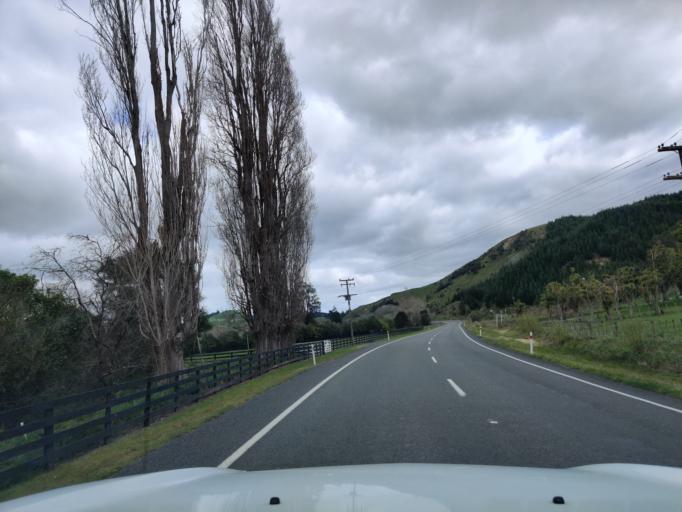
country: NZ
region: Manawatu-Wanganui
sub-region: Wanganui District
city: Wanganui
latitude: -39.8447
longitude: 175.1496
